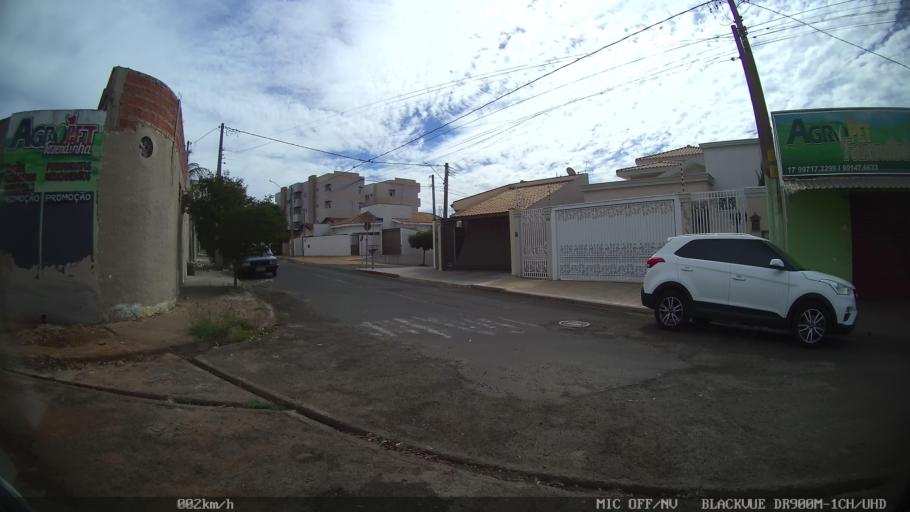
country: BR
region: Sao Paulo
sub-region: Catanduva
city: Catanduva
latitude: -21.1451
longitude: -48.9626
